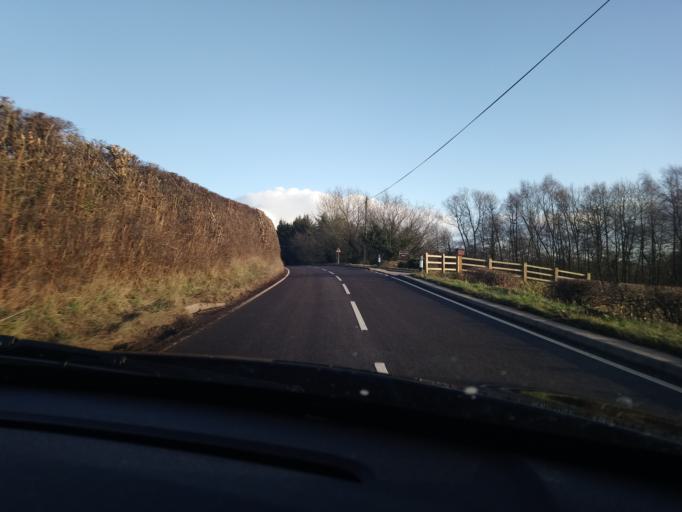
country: GB
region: England
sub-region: Shropshire
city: Ellesmere
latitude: 52.9073
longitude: -2.8282
